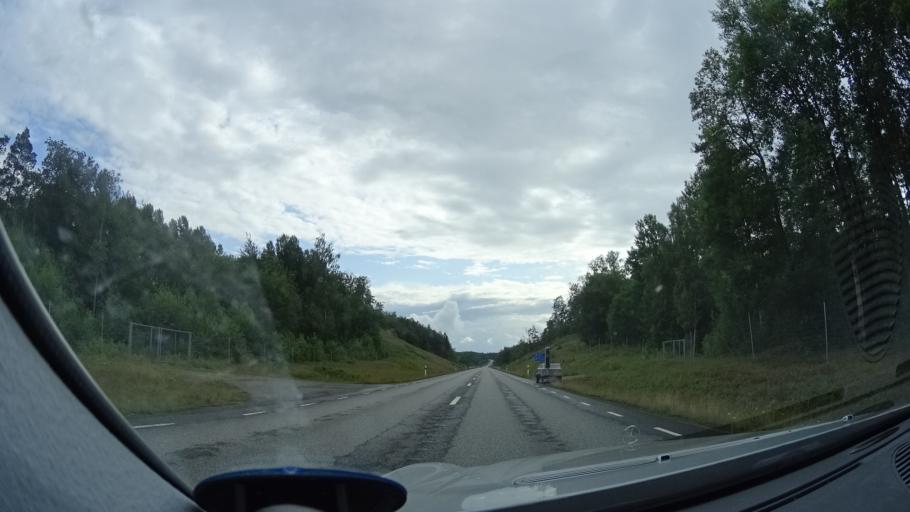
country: SE
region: Blekinge
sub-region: Karlshamns Kommun
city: Svangsta
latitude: 56.2677
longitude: 14.8504
